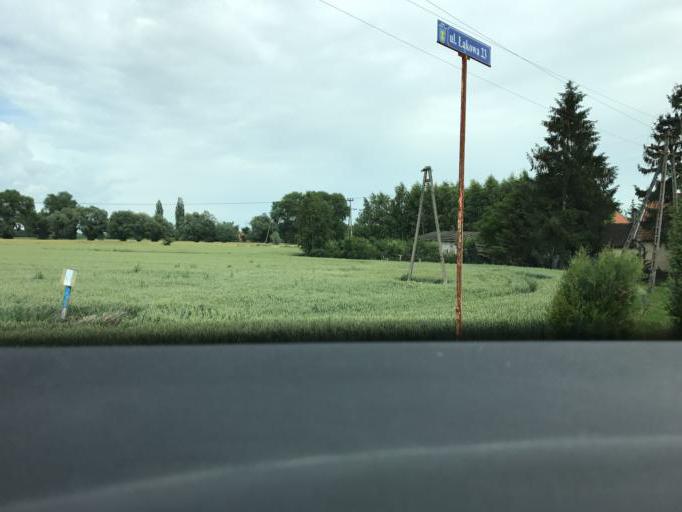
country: PL
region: Pomeranian Voivodeship
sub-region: Powiat gdanski
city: Suchy Dab
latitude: 54.2613
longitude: 18.7378
